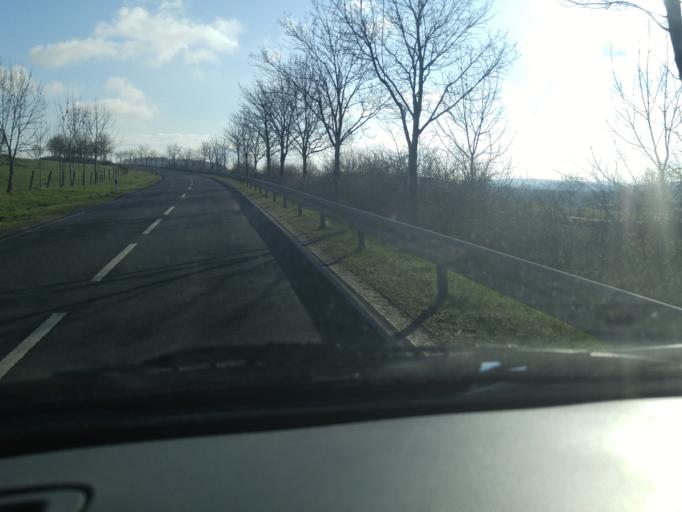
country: DE
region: Hesse
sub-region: Regierungsbezirk Giessen
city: Lautertal
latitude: 50.5890
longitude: 9.2889
